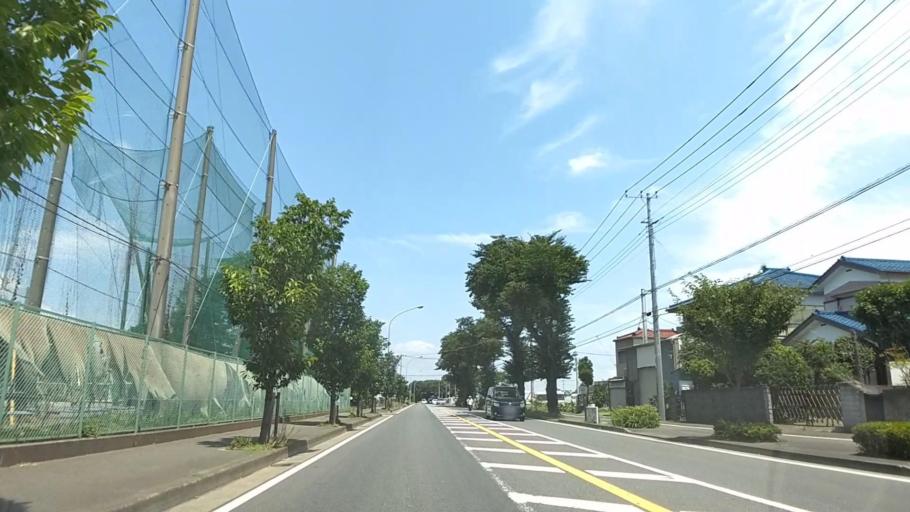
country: JP
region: Kanagawa
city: Minami-rinkan
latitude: 35.4815
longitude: 139.4804
